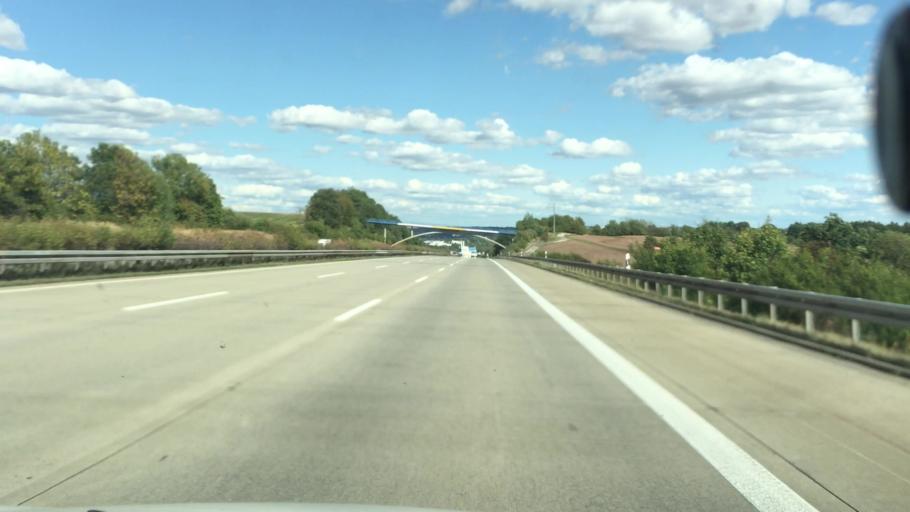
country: DE
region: Thuringia
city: Hartmannsdorf
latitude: 50.9057
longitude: 12.0232
